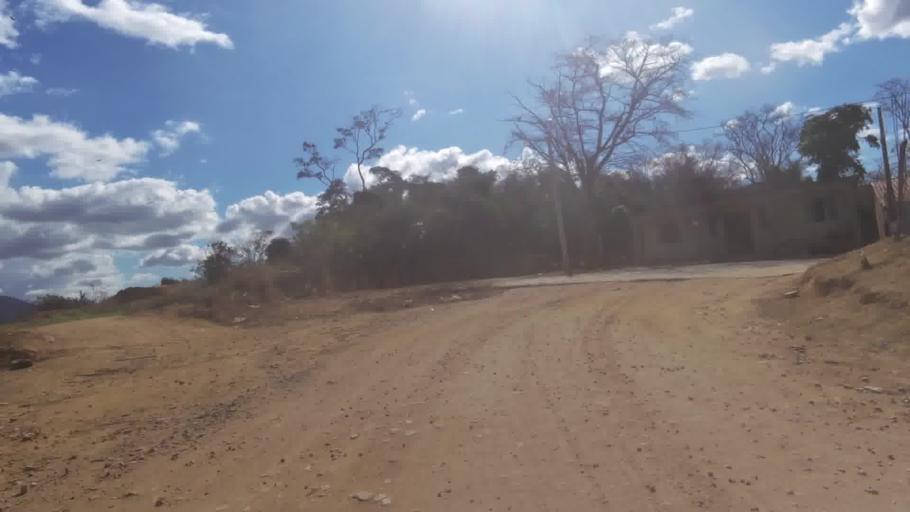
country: BR
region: Espirito Santo
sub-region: Cachoeiro De Itapemirim
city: Cachoeiro de Itapemirim
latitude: -20.9216
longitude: -41.1975
